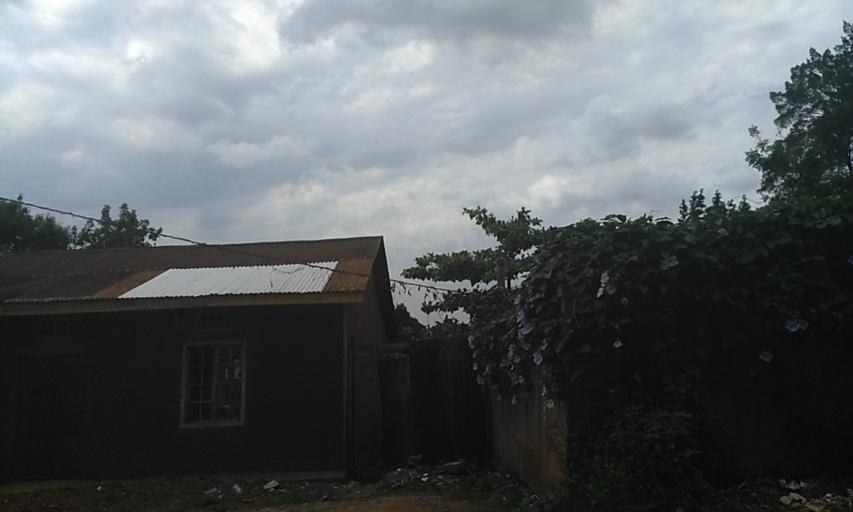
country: UG
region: Central Region
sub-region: Wakiso District
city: Kireka
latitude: 0.3441
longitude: 32.6181
